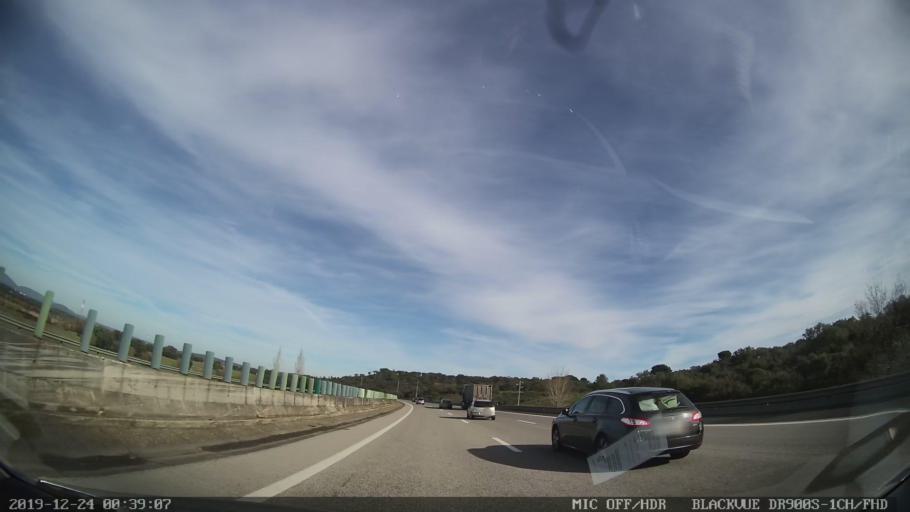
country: PT
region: Lisbon
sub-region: Alenquer
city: Carregado
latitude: 39.0527
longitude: -8.9445
